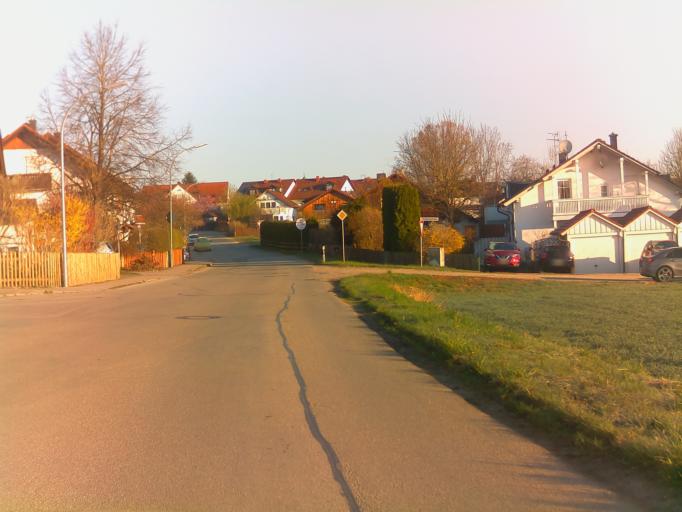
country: DE
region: Bavaria
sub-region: Upper Bavaria
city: Geltendorf
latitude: 48.1198
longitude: 11.0320
